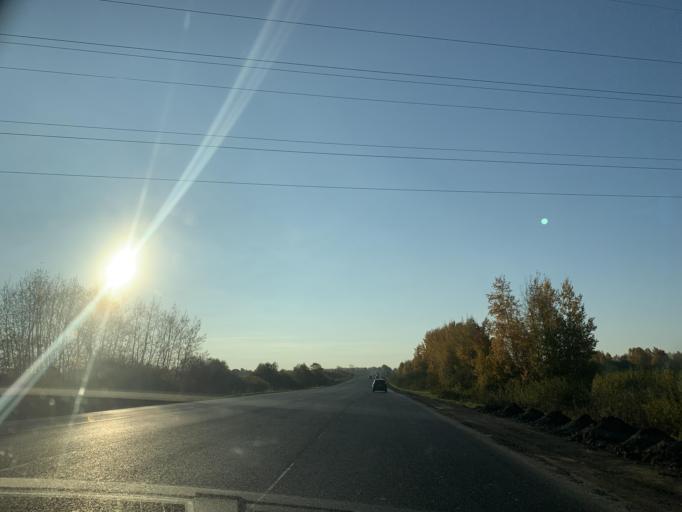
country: RU
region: Jaroslavl
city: Konstantinovskiy
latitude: 57.7999
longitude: 39.5958
